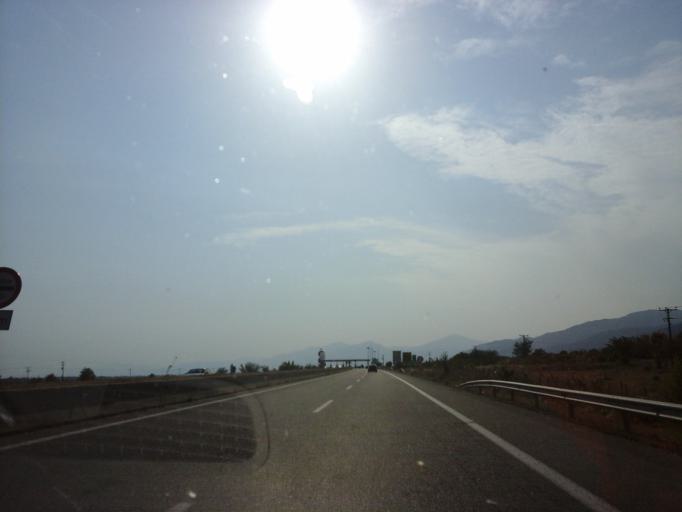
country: GR
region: East Macedonia and Thrace
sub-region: Nomos Xanthis
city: Selero
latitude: 41.1200
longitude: 25.0867
